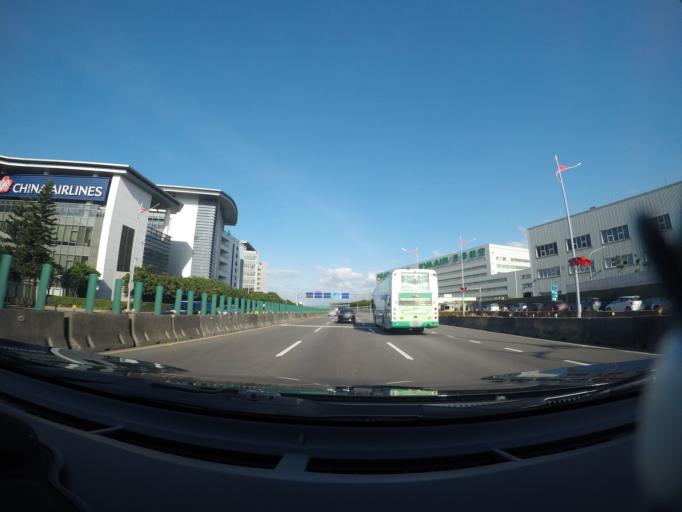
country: TW
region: Taiwan
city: Taoyuan City
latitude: 25.0676
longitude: 121.2201
